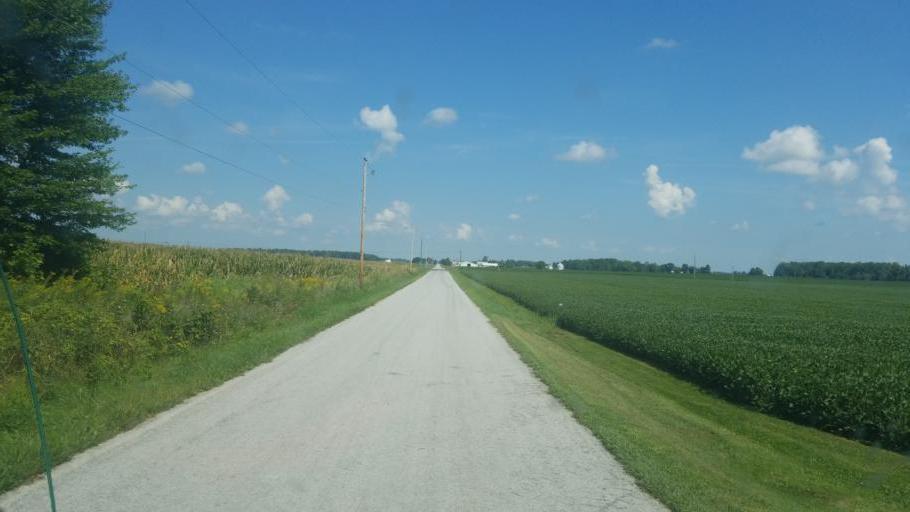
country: US
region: Ohio
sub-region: Hardin County
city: Kenton
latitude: 40.6702
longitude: -83.4957
